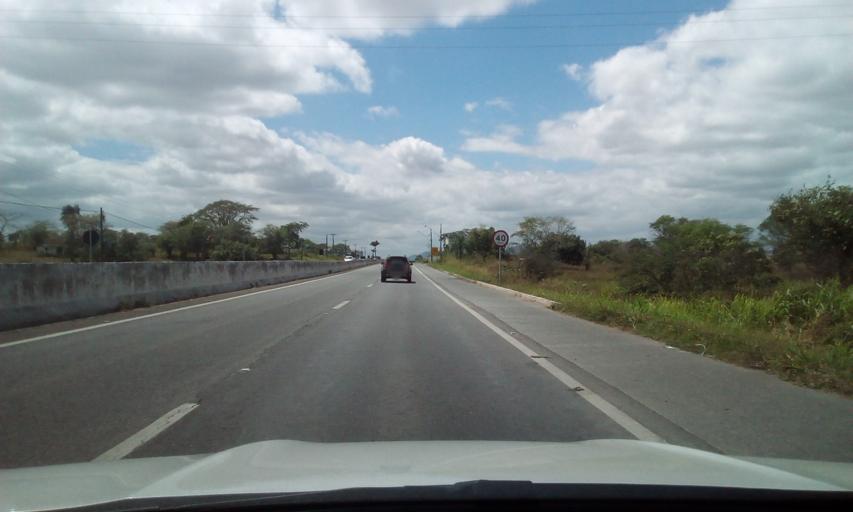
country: BR
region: Paraiba
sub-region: Campina Grande
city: Campina Grande
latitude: -7.2485
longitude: -35.8453
